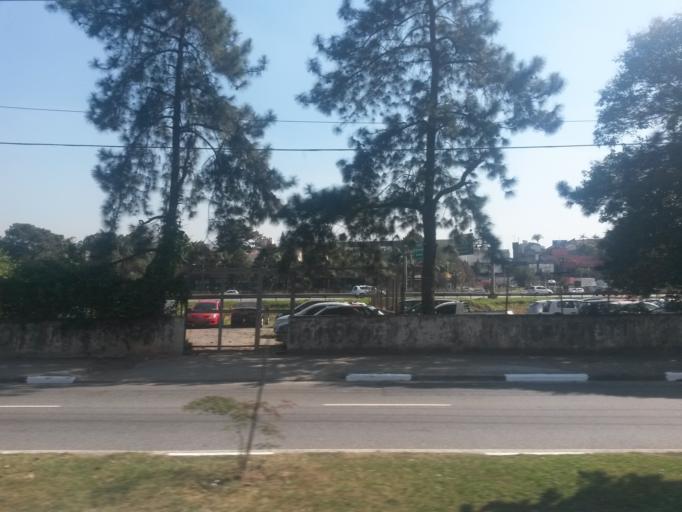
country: BR
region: Sao Paulo
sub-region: Sao Bernardo Do Campo
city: Sao Bernardo do Campo
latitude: -23.7268
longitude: -46.5490
